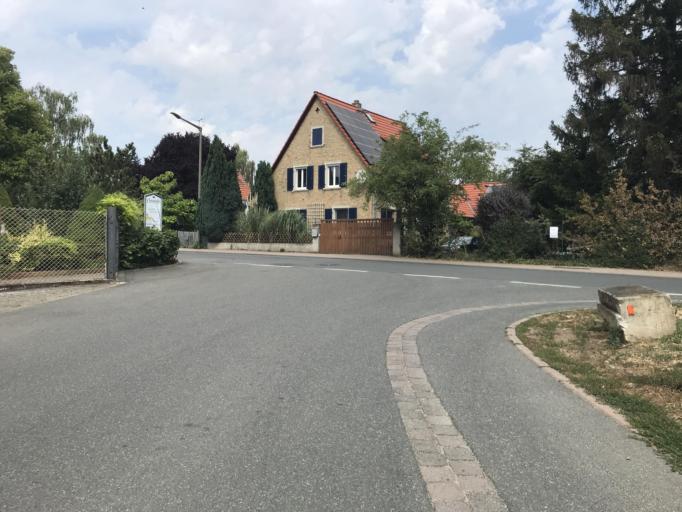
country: DE
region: Rheinland-Pfalz
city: Hahnheim
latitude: 49.8605
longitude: 8.2456
